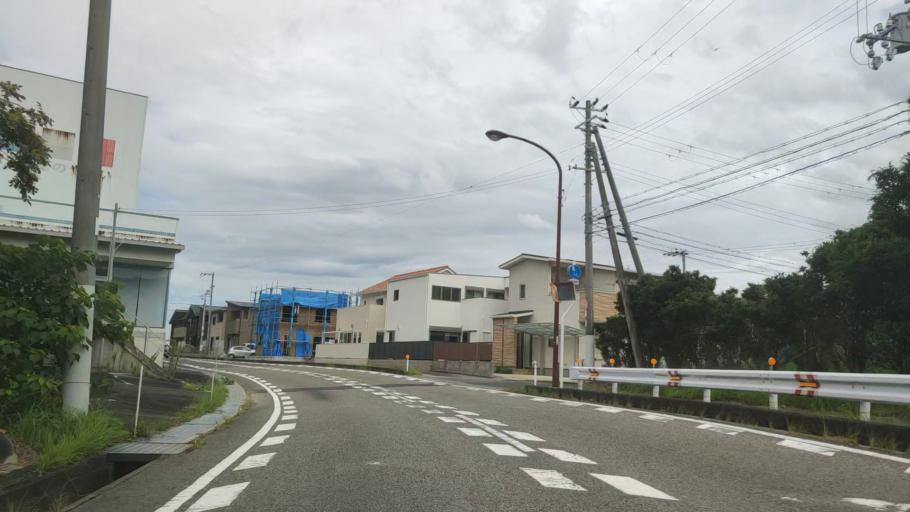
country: JP
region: Wakayama
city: Tanabe
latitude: 33.6870
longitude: 135.3891
